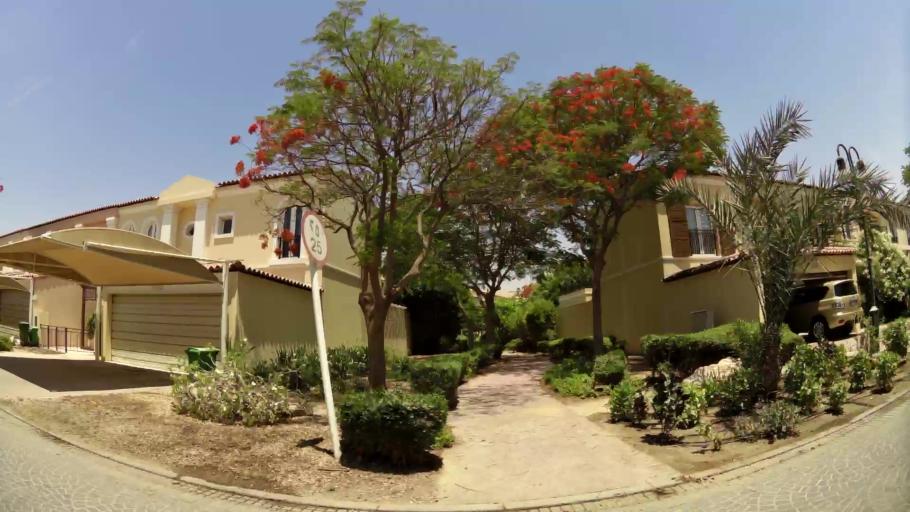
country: AE
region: Dubai
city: Dubai
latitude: 25.0056
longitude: 55.1573
